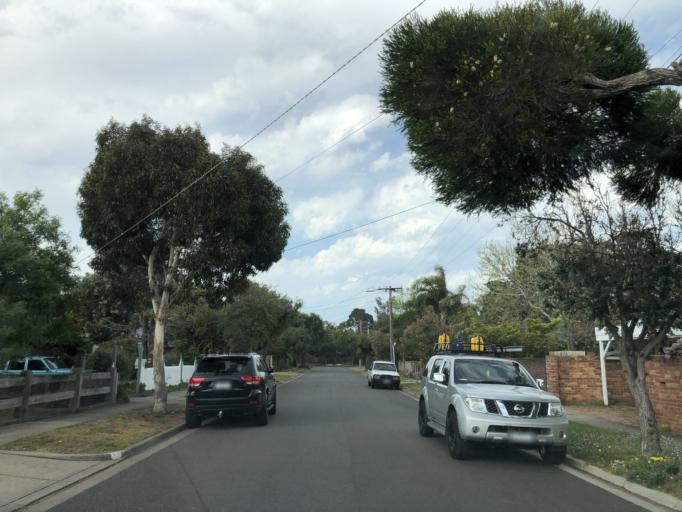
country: AU
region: Victoria
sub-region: Kingston
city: Carrum
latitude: -38.0867
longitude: 145.1286
